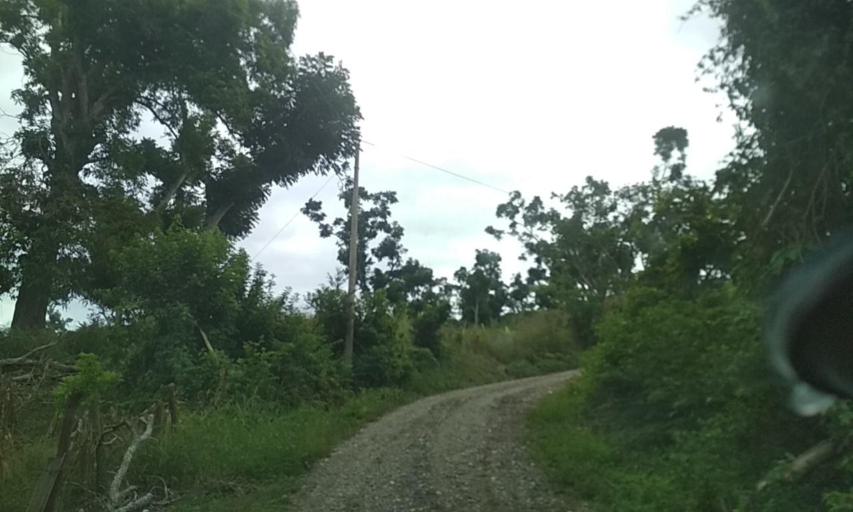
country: MX
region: Veracruz
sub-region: Papantla
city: Polutla
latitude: 20.5848
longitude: -97.2768
